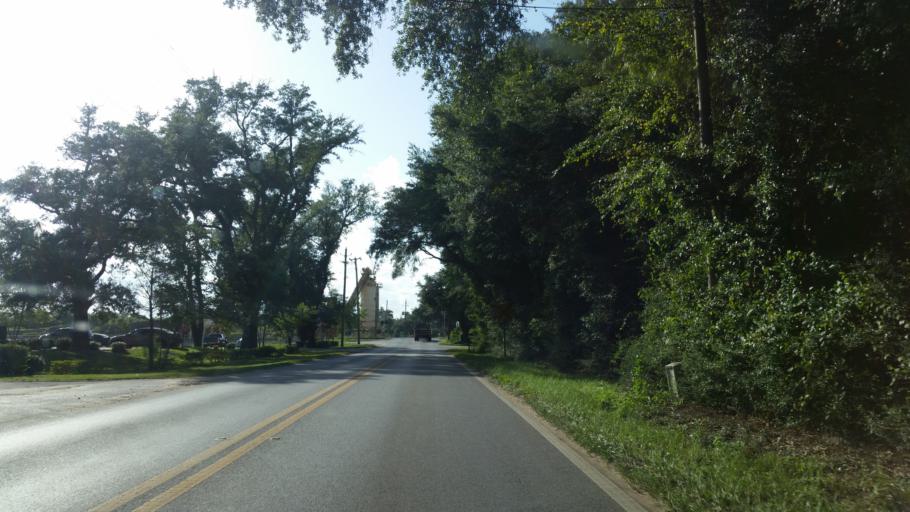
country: US
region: Florida
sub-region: Santa Rosa County
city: Bagdad
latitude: 30.5849
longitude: -87.0617
